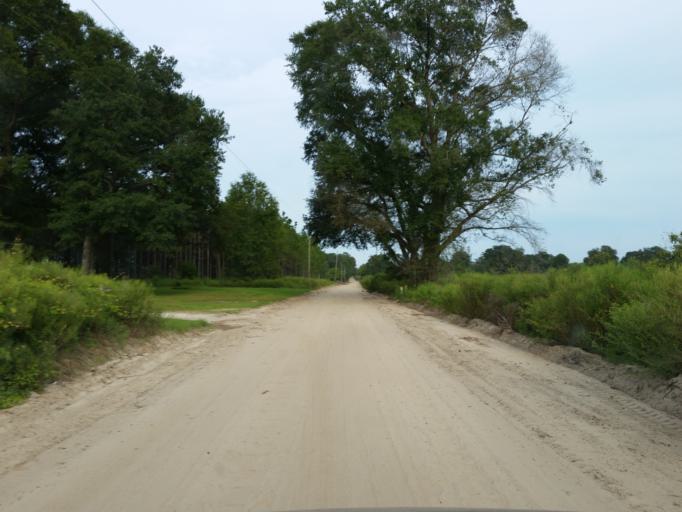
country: US
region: Florida
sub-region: Madison County
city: Madison
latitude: 30.5375
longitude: -83.2057
